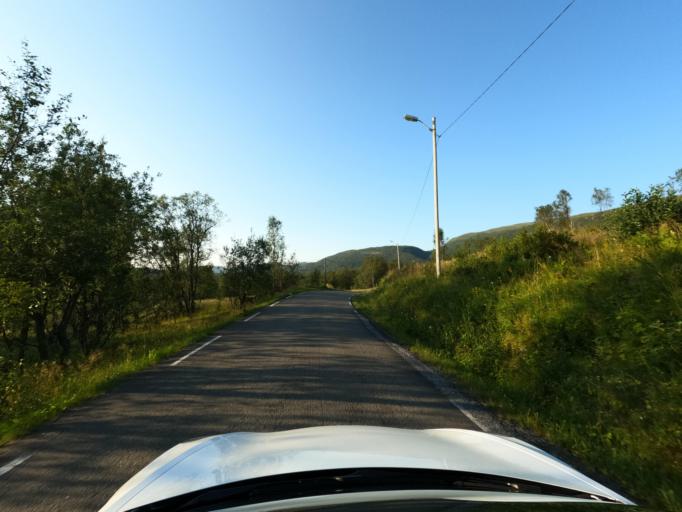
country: NO
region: Nordland
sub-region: Ballangen
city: Ballangen
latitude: 68.5228
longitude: 16.7629
